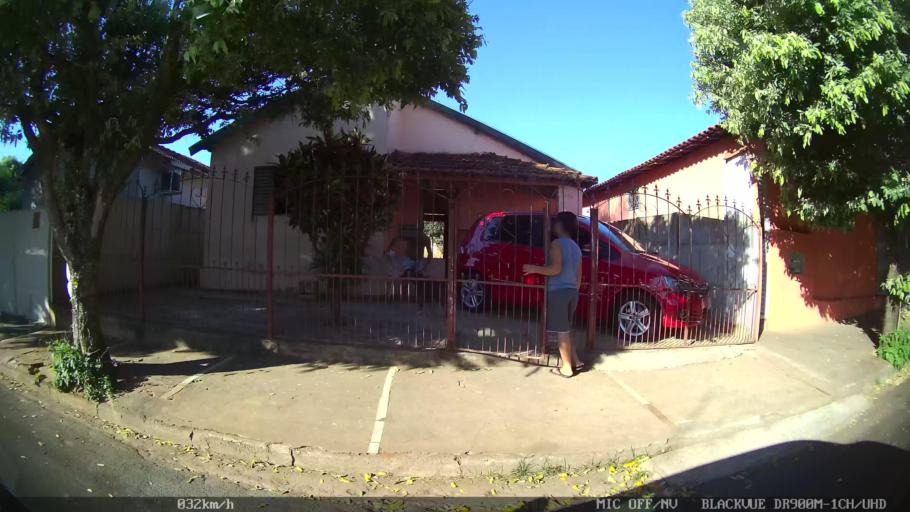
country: BR
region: Sao Paulo
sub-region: Olimpia
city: Olimpia
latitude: -20.7322
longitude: -48.9083
